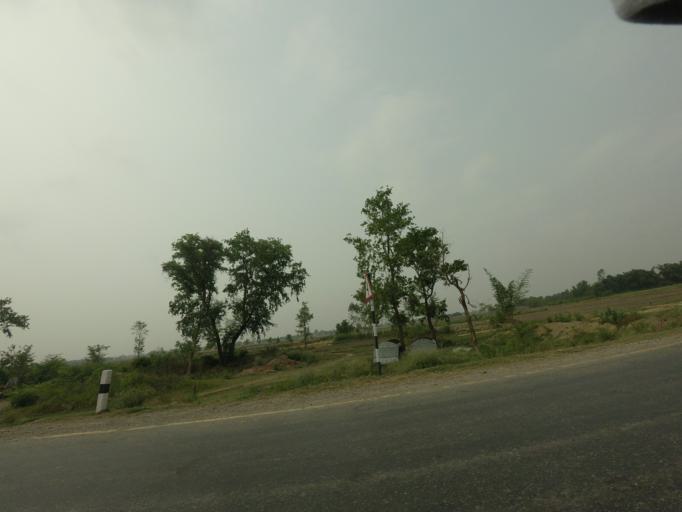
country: IN
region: Uttar Pradesh
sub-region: Maharajganj
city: Nautanwa
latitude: 27.4911
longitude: 83.2996
